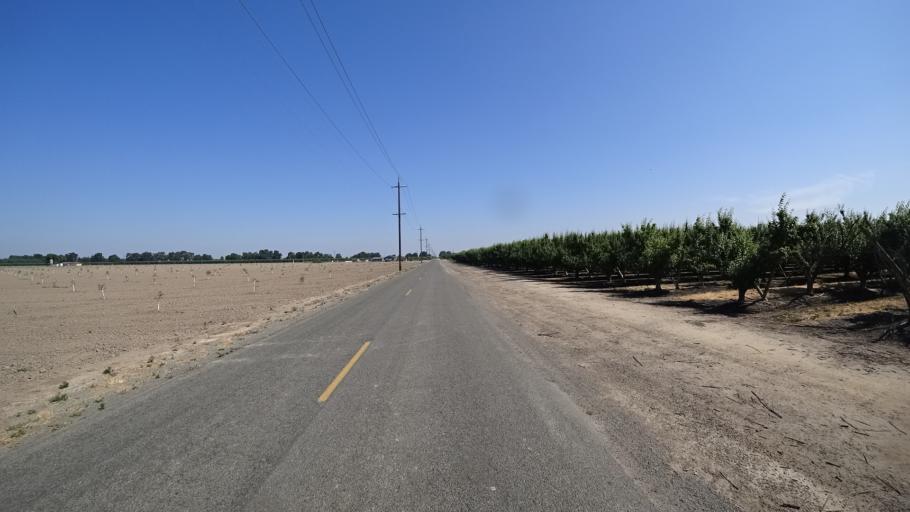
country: US
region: California
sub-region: Fresno County
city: Kingsburg
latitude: 36.4268
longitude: -119.5828
